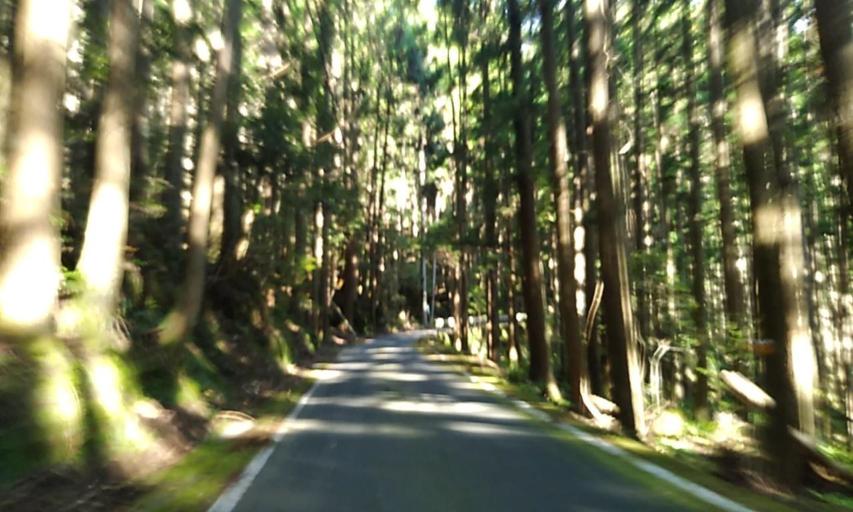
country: JP
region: Wakayama
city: Shingu
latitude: 33.9124
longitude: 135.9892
